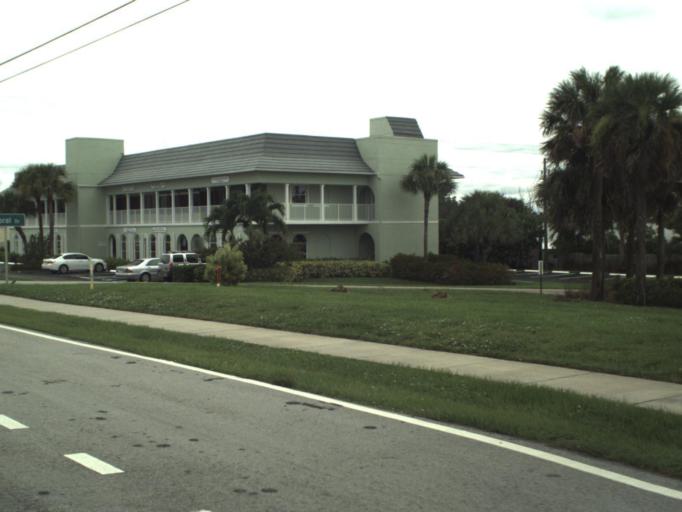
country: US
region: Florida
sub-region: Palm Beach County
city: Juno Beach
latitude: 26.8806
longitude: -80.0562
